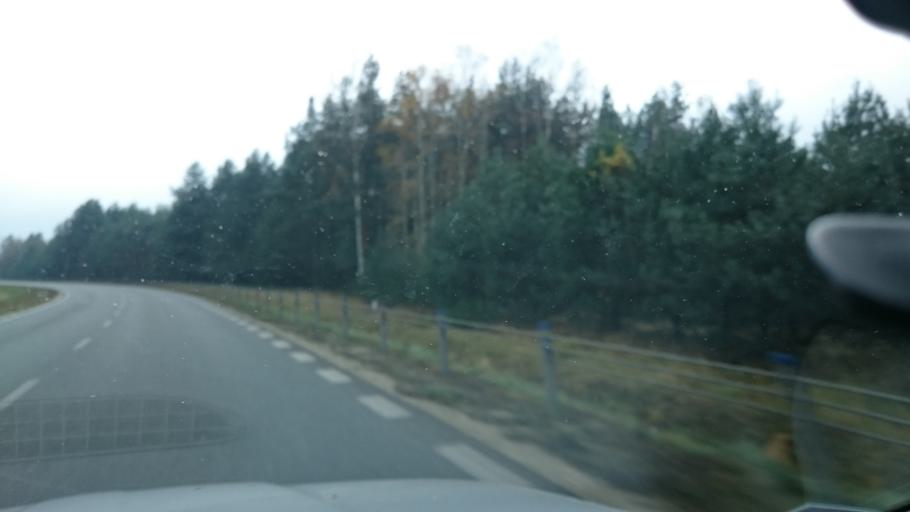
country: PL
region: Swietokrzyskie
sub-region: Powiat konecki
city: Konskie
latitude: 51.1515
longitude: 20.3618
